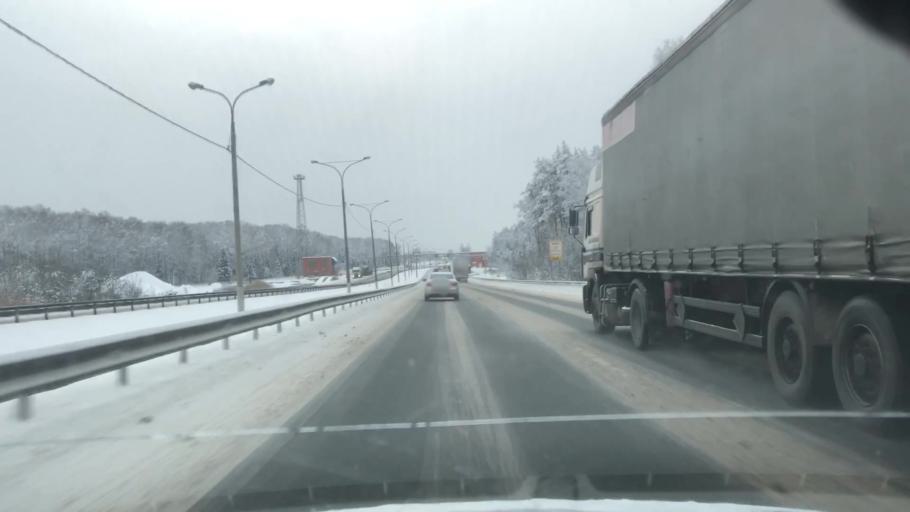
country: RU
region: Moskovskaya
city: Mikhnevo
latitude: 55.1368
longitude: 37.9329
